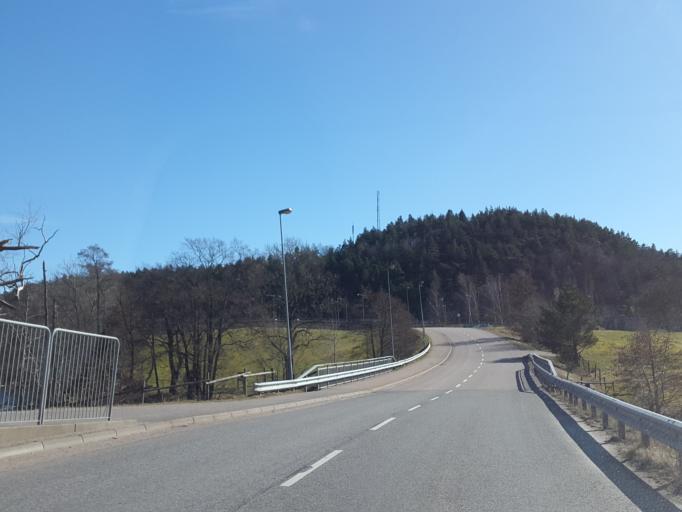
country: SE
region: Vaestra Goetaland
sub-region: Partille Kommun
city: Furulund
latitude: 57.7466
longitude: 12.1577
